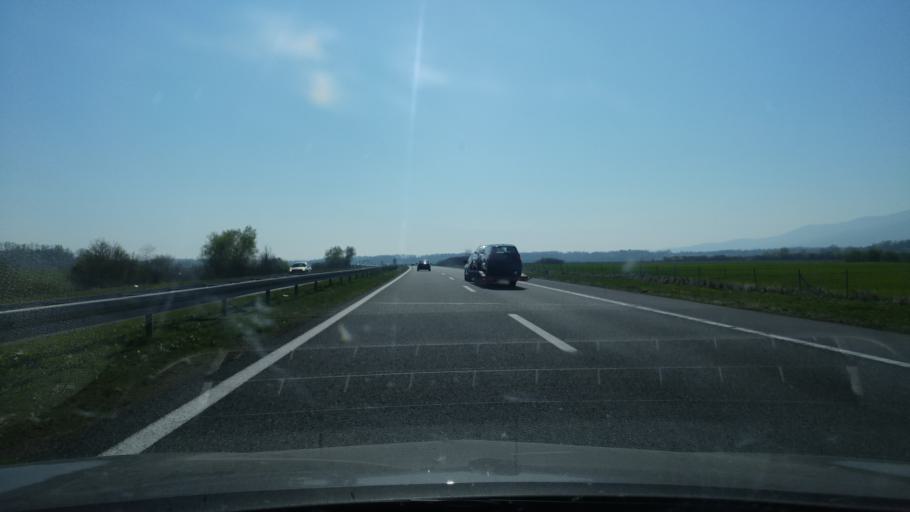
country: HR
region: Brodsko-Posavska
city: Batrina
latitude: 45.1768
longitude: 17.6515
